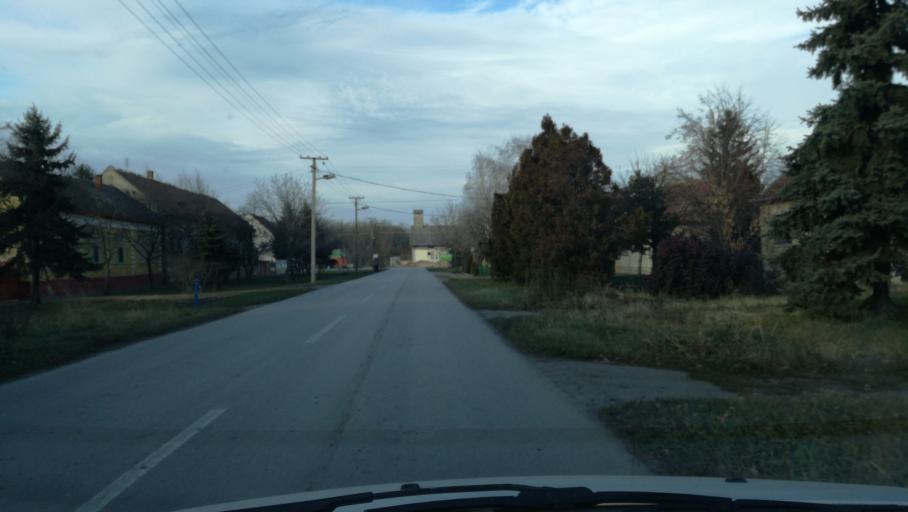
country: RS
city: Banatsko Veliko Selo
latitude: 45.8185
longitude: 20.6077
